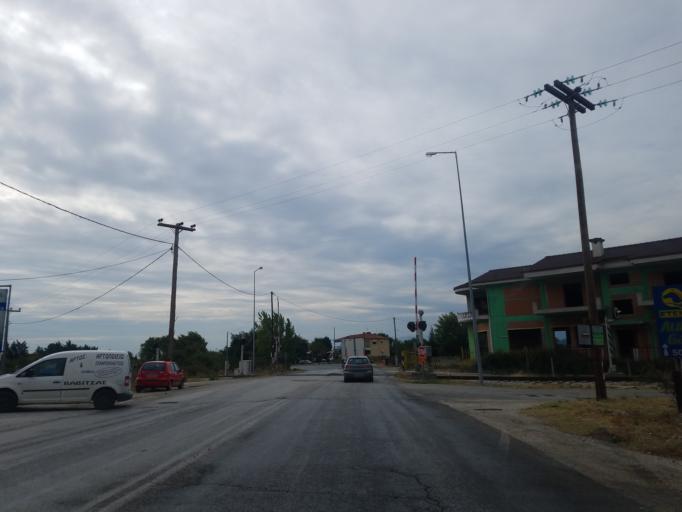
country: GR
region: Thessaly
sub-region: Trikala
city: Kalampaka
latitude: 39.6970
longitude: 21.6401
